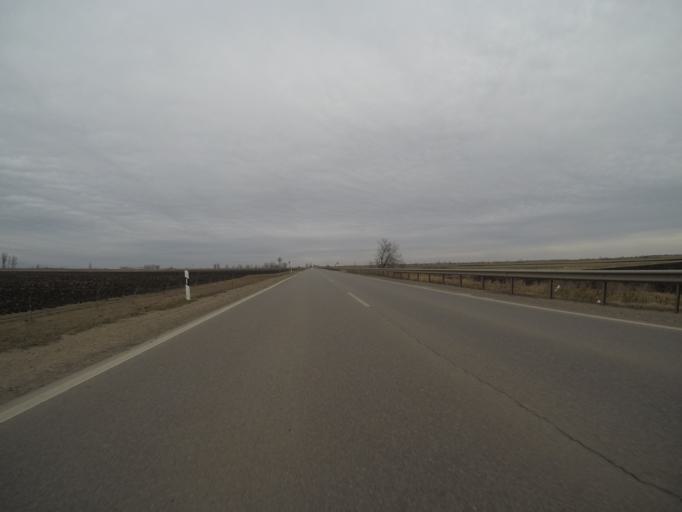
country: HU
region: Jasz-Nagykun-Szolnok
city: Jaszjakohalma
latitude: 47.5160
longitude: 19.9546
